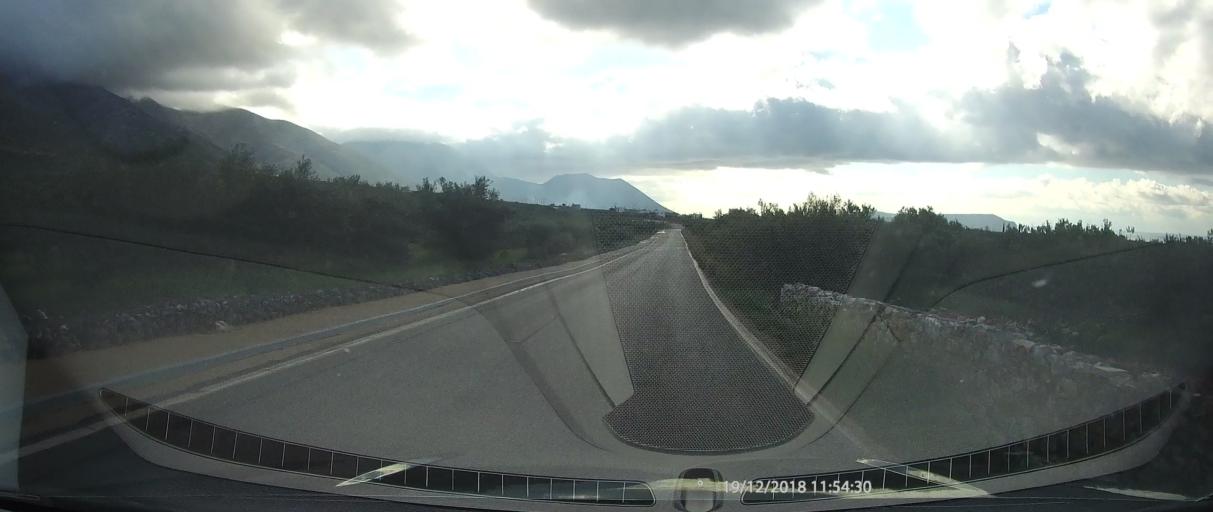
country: GR
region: Peloponnese
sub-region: Nomos Lakonias
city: Gytheio
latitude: 36.6177
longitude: 22.3908
